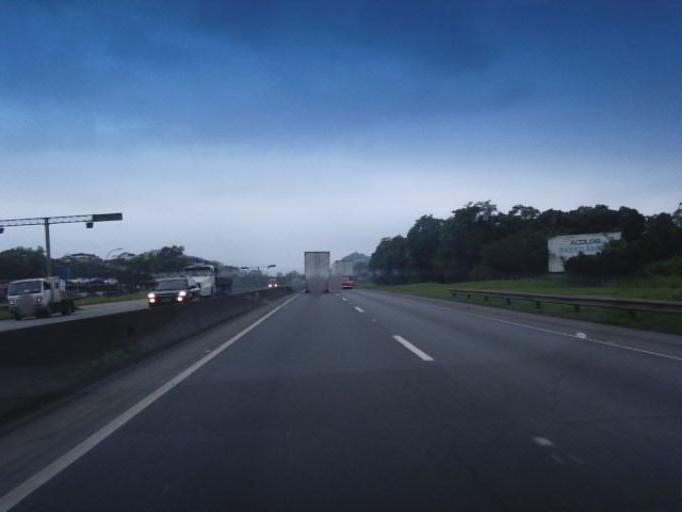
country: BR
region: Santa Catarina
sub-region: Joinville
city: Joinville
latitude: -26.0988
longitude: -48.8681
